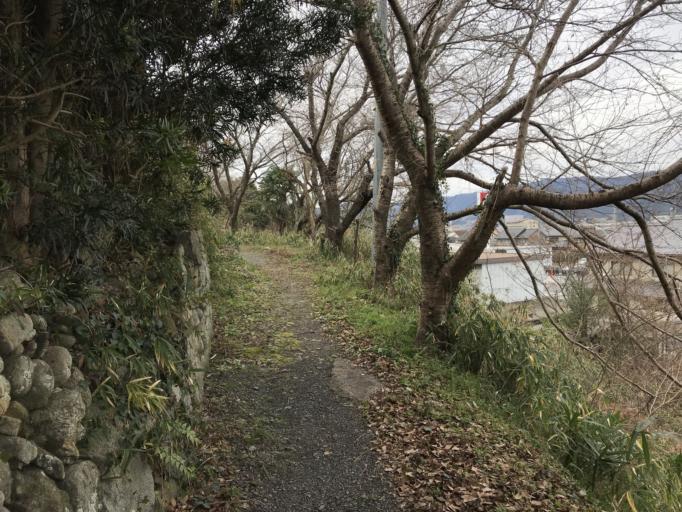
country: JP
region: Mie
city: Ueno-ebisumachi
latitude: 34.7696
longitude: 136.1418
